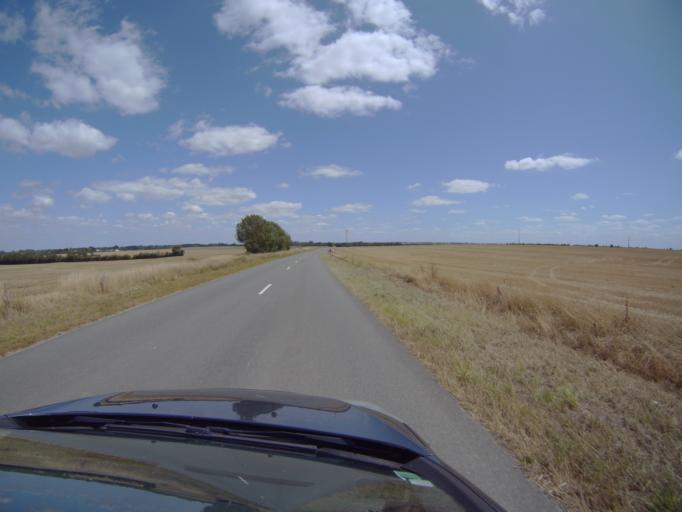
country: FR
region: Poitou-Charentes
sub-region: Departement des Deux-Sevres
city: Saint-Hilaire-la-Palud
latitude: 46.2704
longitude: -0.6565
